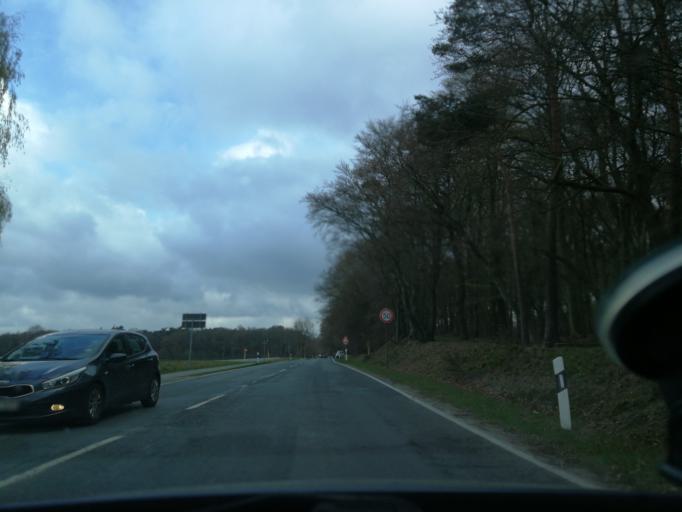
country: DE
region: Lower Saxony
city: Seevetal
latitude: 53.4376
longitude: 9.9149
